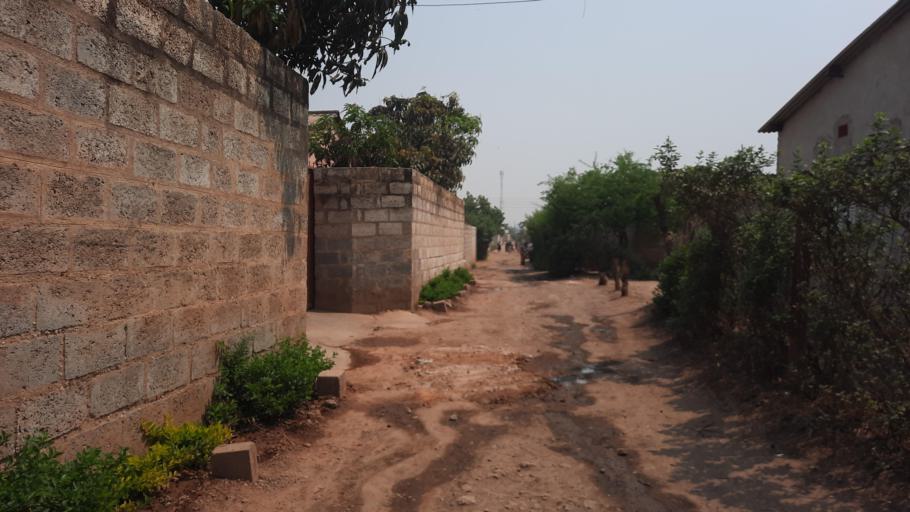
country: ZM
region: Lusaka
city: Lusaka
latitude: -15.3997
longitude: 28.3793
